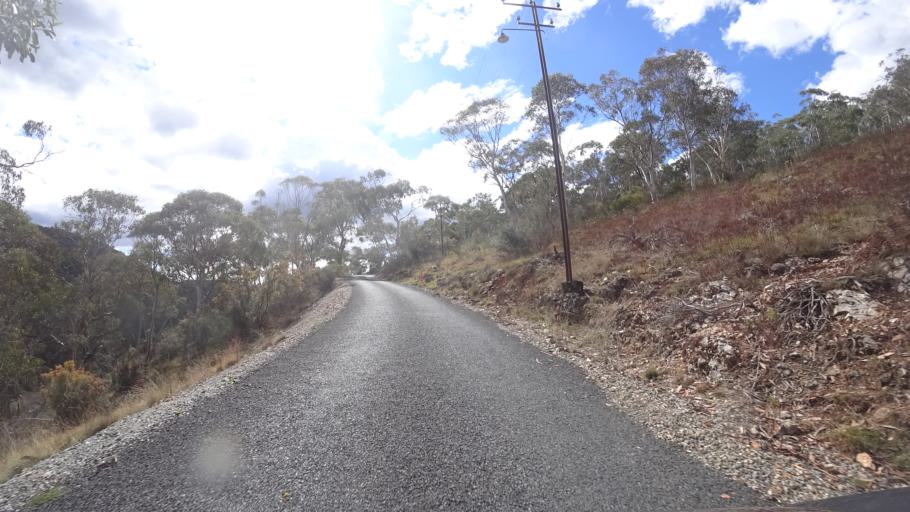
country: AU
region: New South Wales
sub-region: Tumut Shire
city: Tumut
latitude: -35.7250
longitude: 148.4881
